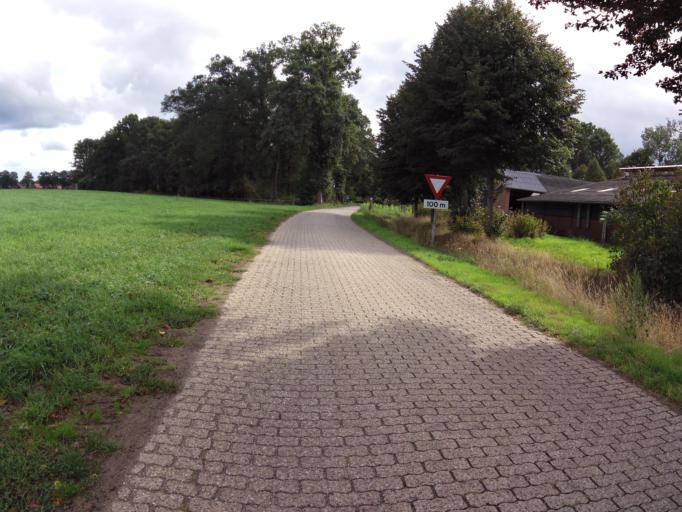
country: NL
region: Gelderland
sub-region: Gemeente Aalten
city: Bredevoort
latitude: 51.9713
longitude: 6.6524
